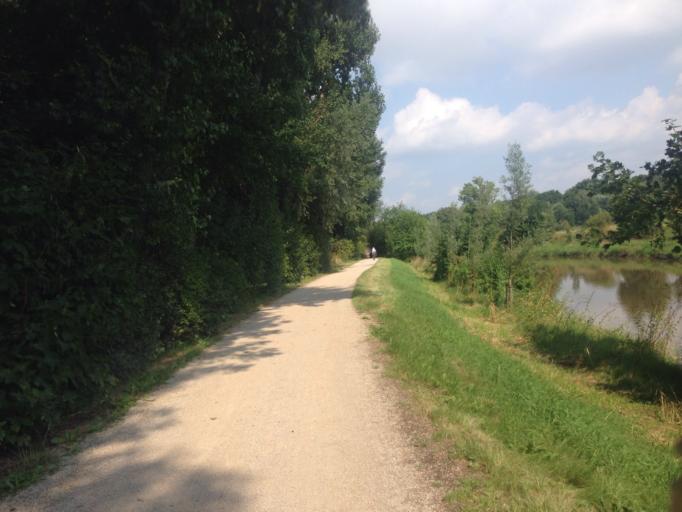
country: DE
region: Hesse
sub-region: Regierungsbezirk Darmstadt
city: Frankfurt am Main
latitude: 50.1763
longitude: 8.6748
